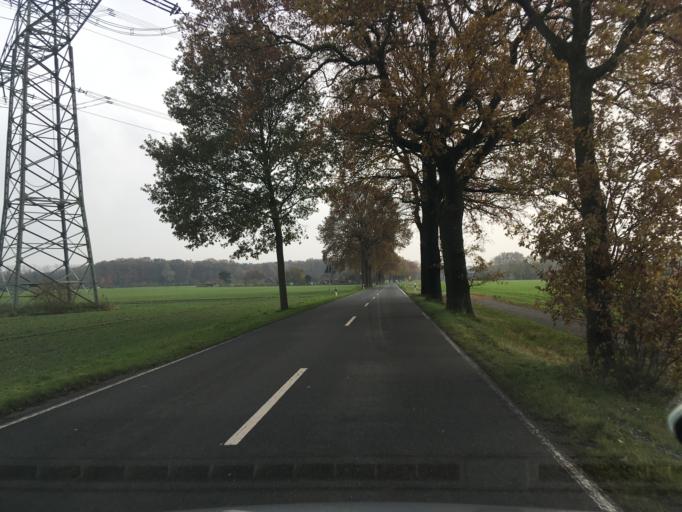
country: DE
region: North Rhine-Westphalia
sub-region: Regierungsbezirk Munster
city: Velen
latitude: 51.9051
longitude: 6.9719
